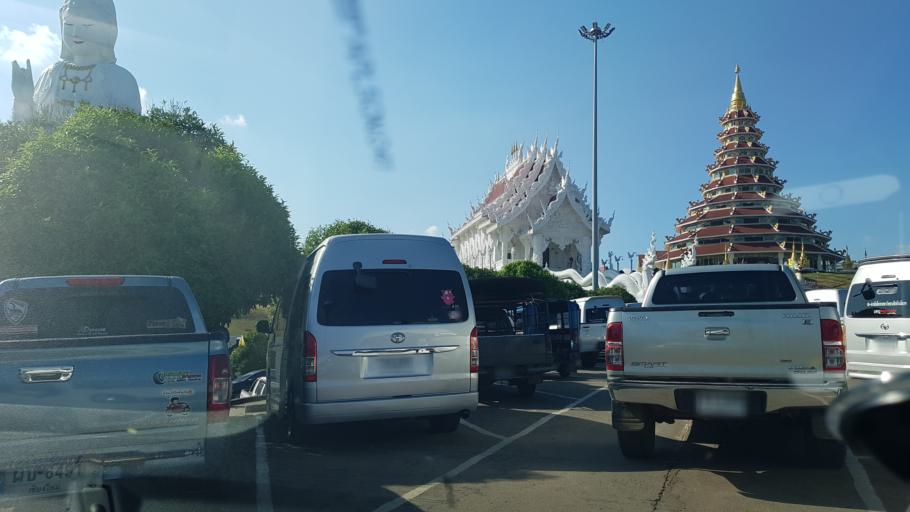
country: TH
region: Chiang Rai
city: Chiang Rai
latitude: 19.9489
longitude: 99.8075
